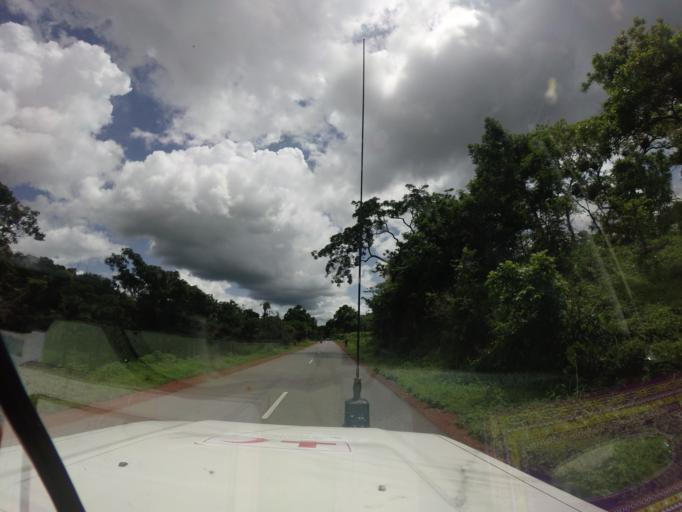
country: SL
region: Northern Province
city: Bindi
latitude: 10.1523
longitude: -11.5394
